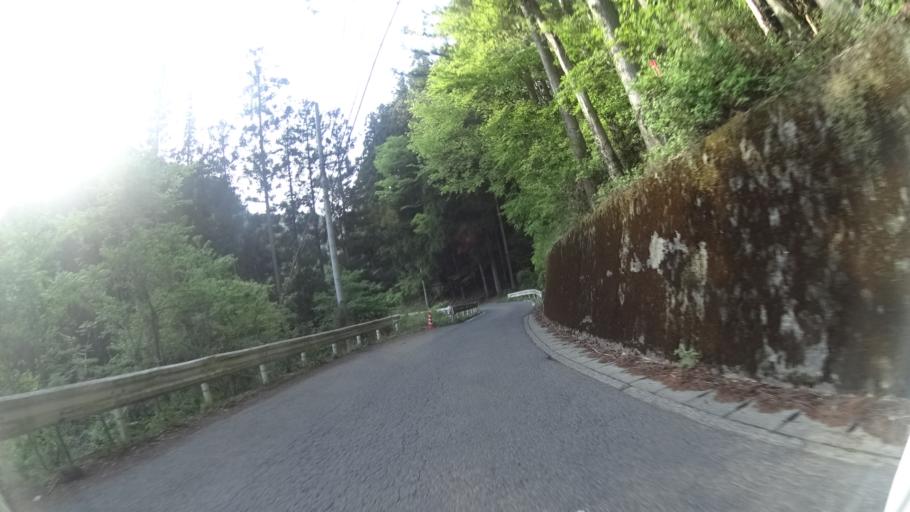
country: JP
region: Tokushima
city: Ikedacho
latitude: 33.8670
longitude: 133.9447
